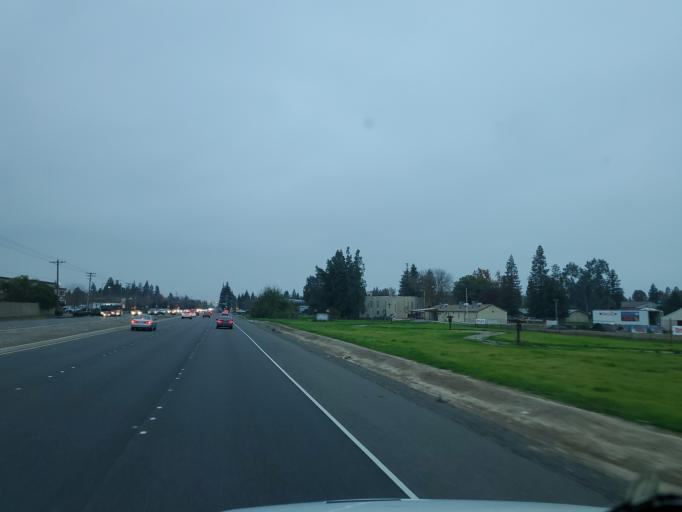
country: US
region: California
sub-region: Stanislaus County
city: Salida
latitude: 37.7005
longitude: -121.0462
